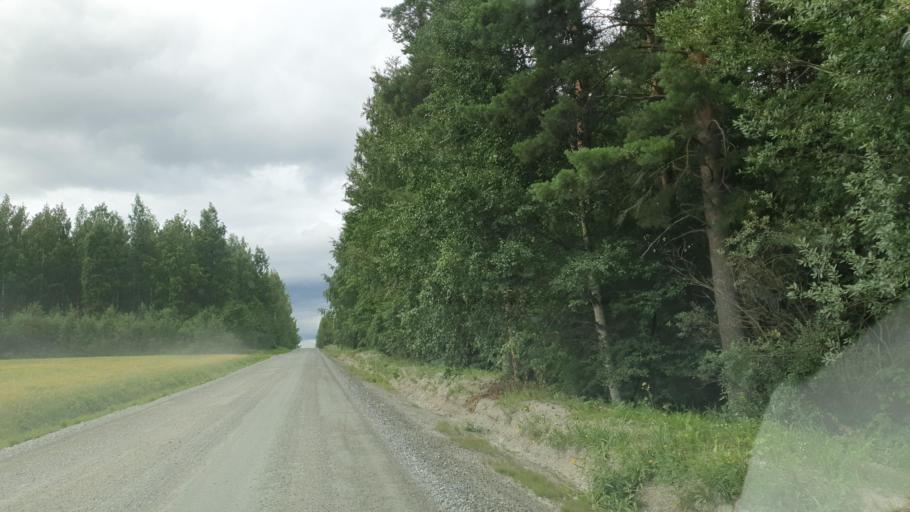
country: FI
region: Northern Savo
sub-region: Ylae-Savo
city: Iisalmi
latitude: 63.5222
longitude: 27.0959
